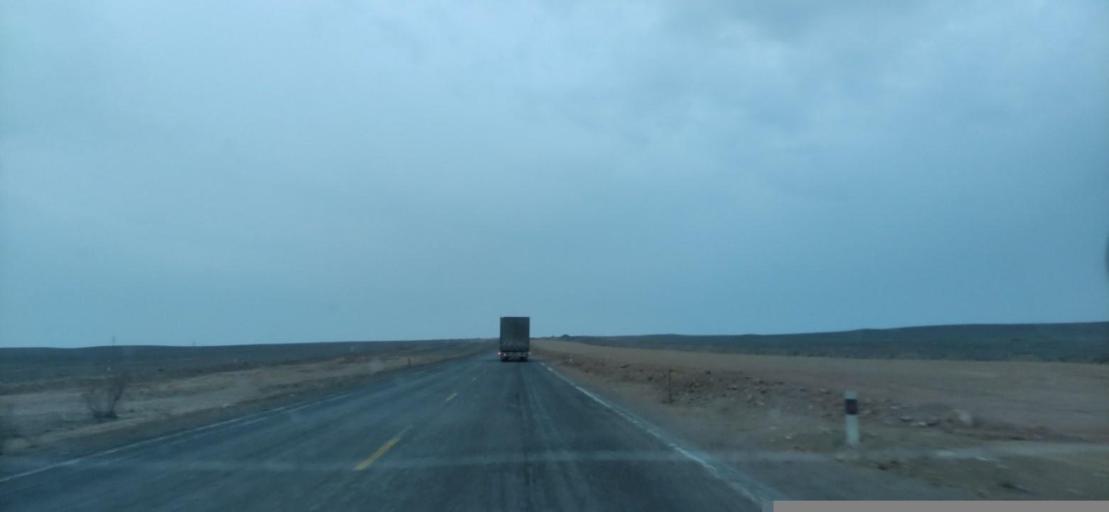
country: KZ
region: Qaraghandy
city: Saryshaghan
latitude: 46.1745
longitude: 73.6214
